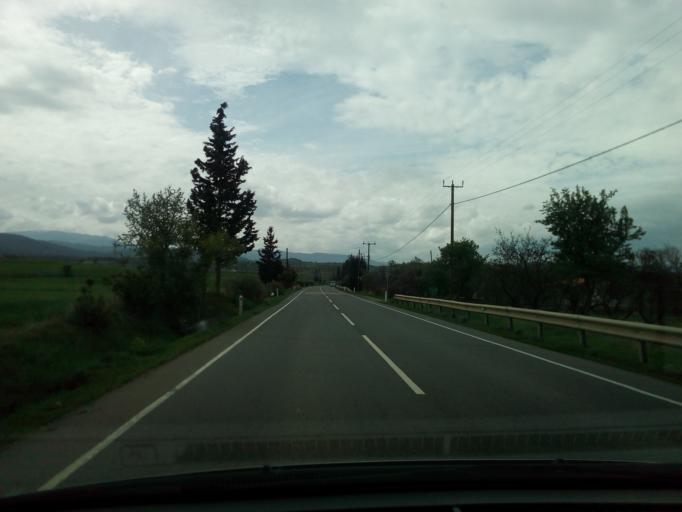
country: CY
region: Lefkosia
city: Astromeritis
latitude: 35.0865
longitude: 32.9585
